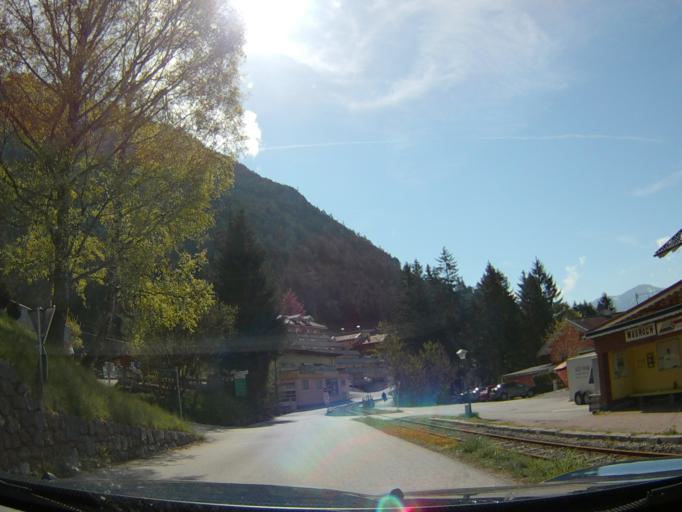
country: AT
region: Tyrol
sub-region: Politischer Bezirk Schwaz
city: Jenbach
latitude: 47.4218
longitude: 11.7536
